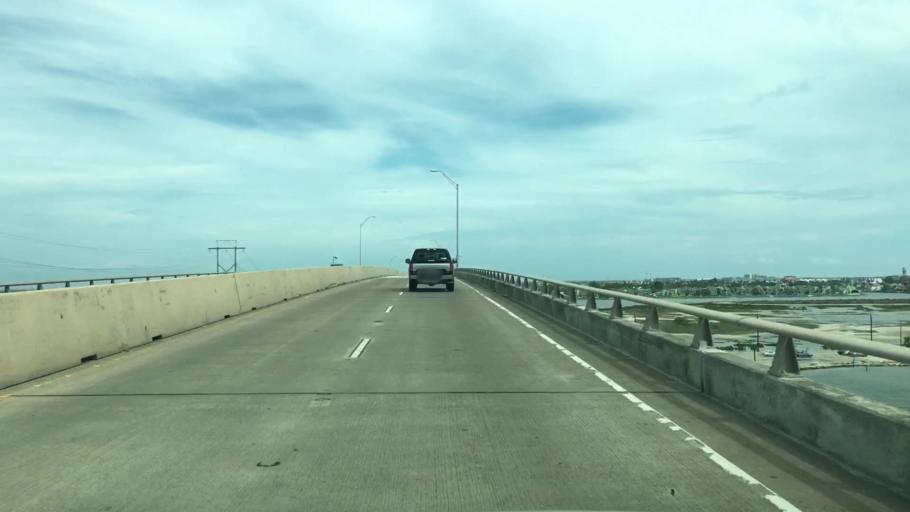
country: US
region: Texas
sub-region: Nueces County
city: Corpus Christi
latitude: 27.6353
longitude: -97.2411
